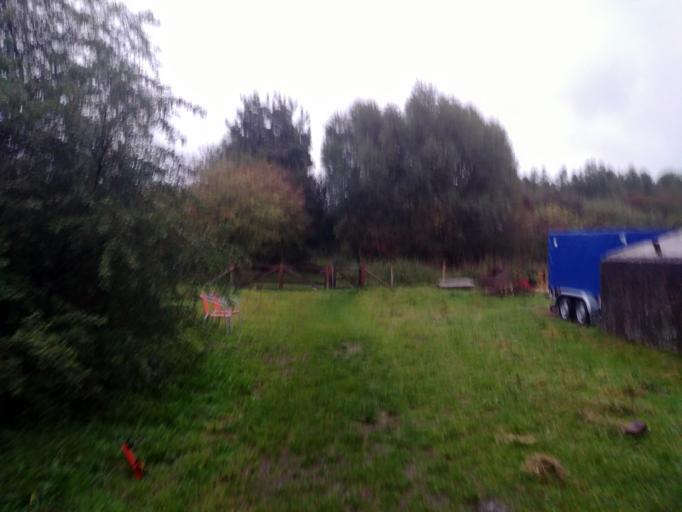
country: NL
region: Gelderland
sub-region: Gemeente Wageningen
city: Wageningen
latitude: 51.9573
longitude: 5.6663
